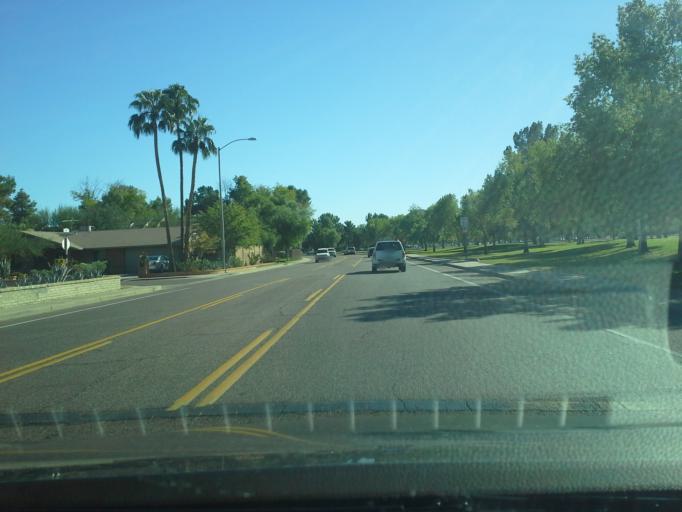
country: US
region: Arizona
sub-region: Maricopa County
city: Paradise Valley
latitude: 33.6072
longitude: -111.9866
